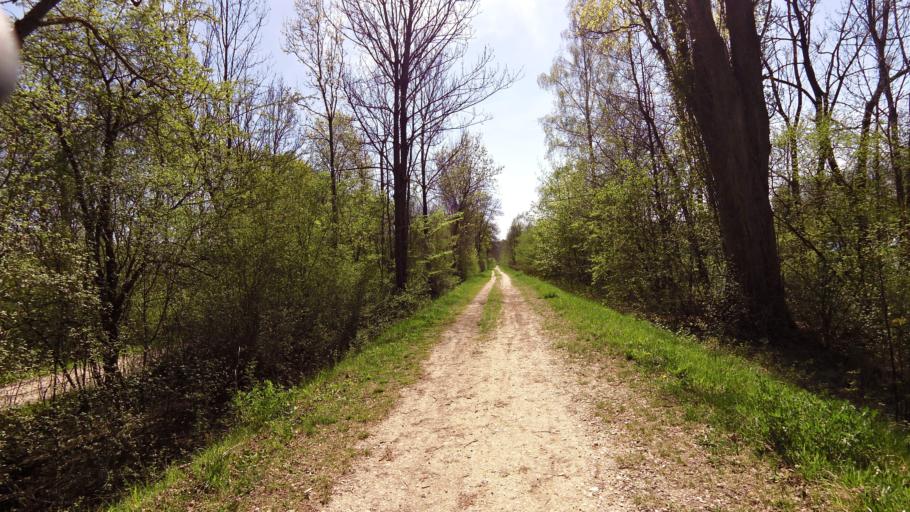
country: DE
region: Bavaria
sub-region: Lower Bavaria
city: Ergolding
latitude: 48.5568
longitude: 12.1822
